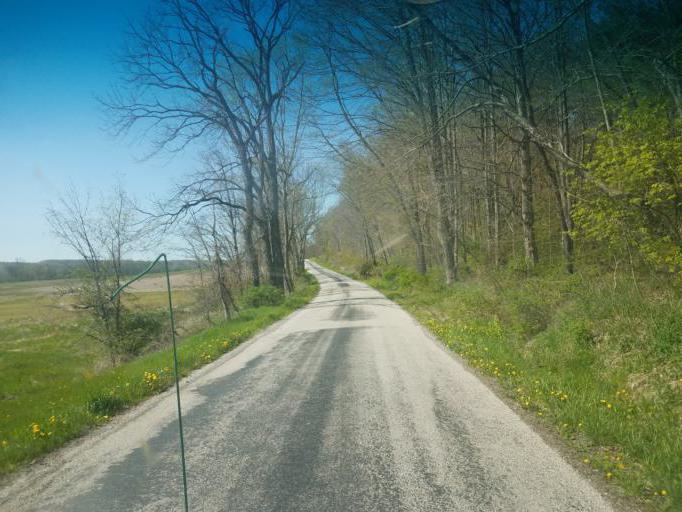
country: US
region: Ohio
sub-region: Medina County
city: Lodi
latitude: 40.9443
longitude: -82.0162
